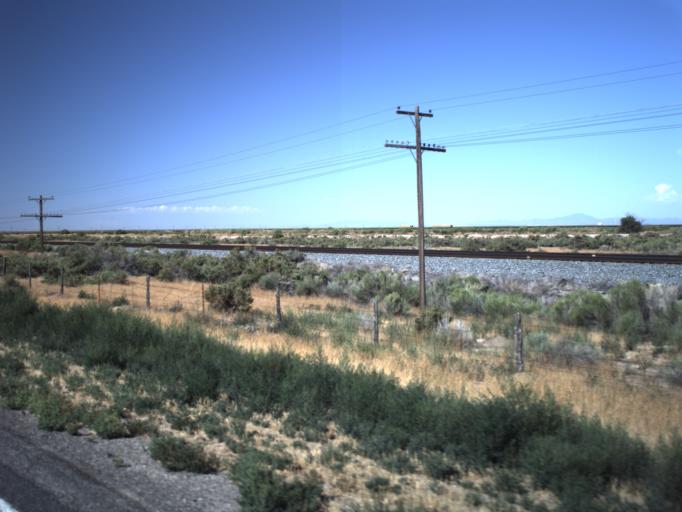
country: US
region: Utah
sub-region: Millard County
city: Delta
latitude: 39.5378
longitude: -112.3649
